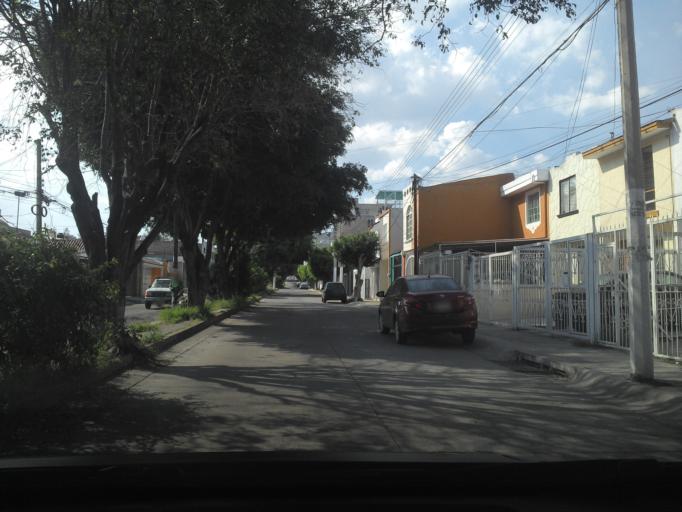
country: MX
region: Jalisco
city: Guadalajara
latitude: 20.6482
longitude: -103.4406
